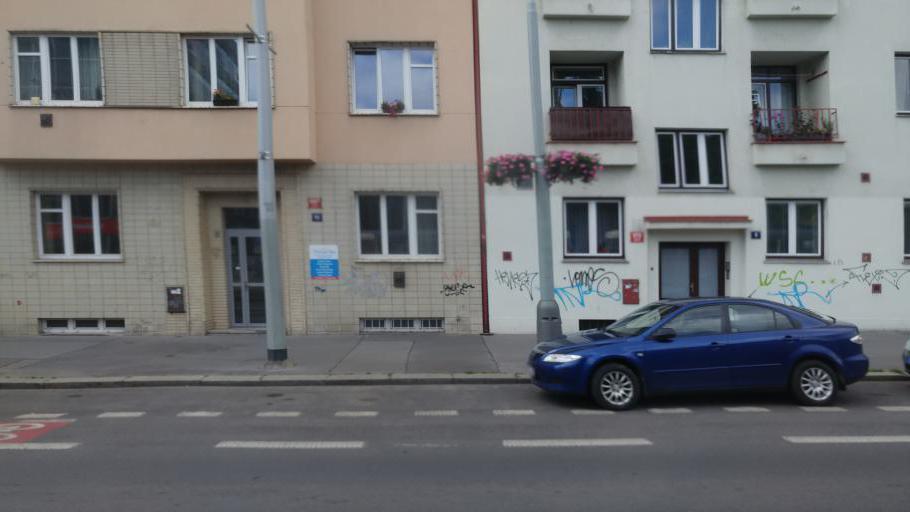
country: CZ
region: Praha
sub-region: Praha 8
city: Liben
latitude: 50.0710
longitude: 14.4808
